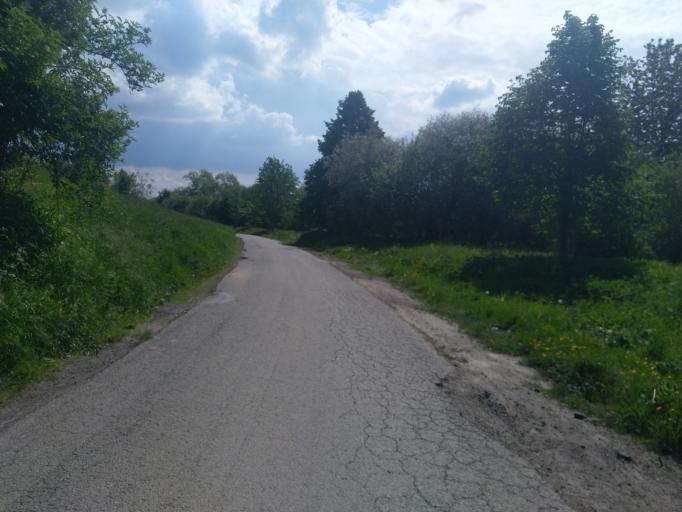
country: BE
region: Wallonia
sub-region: Province du Hainaut
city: Chasse Royale
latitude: 50.4178
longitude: 3.9694
